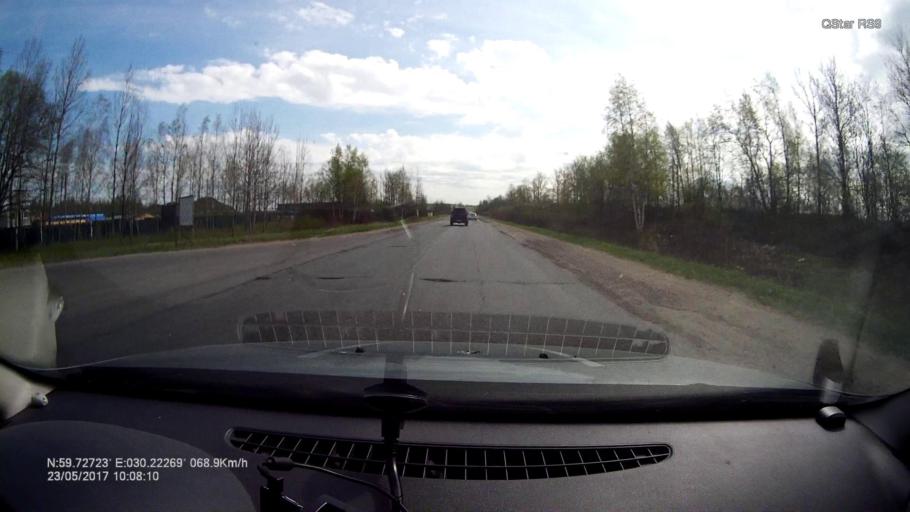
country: RU
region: St.-Petersburg
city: Aleksandrovskaya
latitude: 59.7272
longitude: 30.2230
